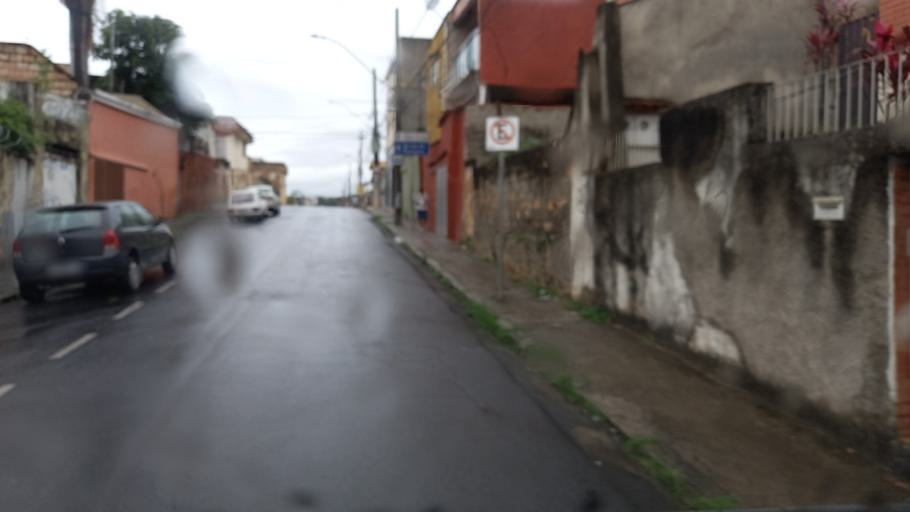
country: BR
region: Minas Gerais
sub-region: Belo Horizonte
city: Belo Horizonte
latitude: -19.9145
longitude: -43.9049
